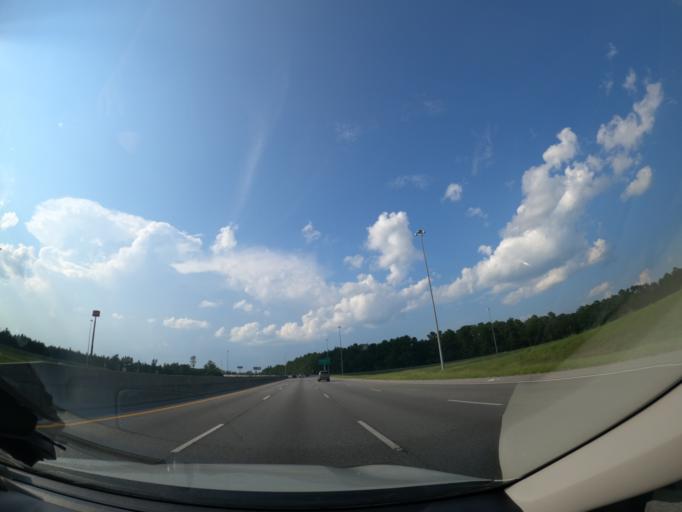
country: US
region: Georgia
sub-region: Columbia County
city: Martinez
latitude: 33.4510
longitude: -82.0736
